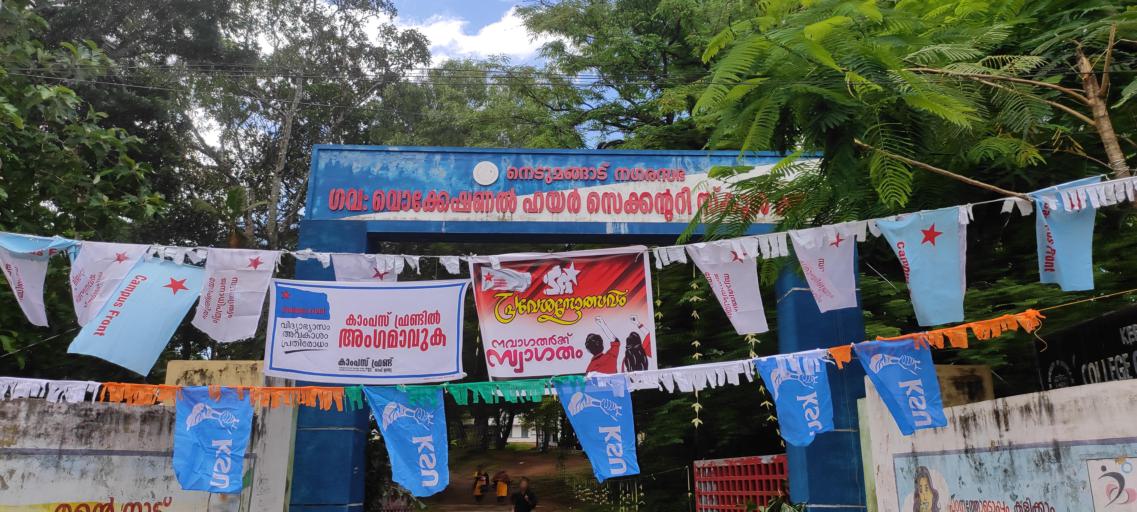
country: IN
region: Kerala
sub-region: Thiruvananthapuram
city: Nedumangad
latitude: 8.5977
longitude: 77.0081
